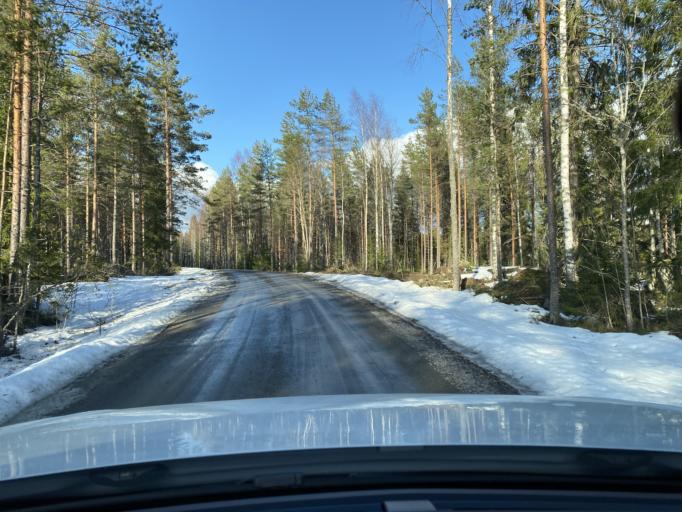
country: FI
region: Pirkanmaa
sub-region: Lounais-Pirkanmaa
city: Mouhijaervi
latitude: 61.4568
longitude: 22.9461
